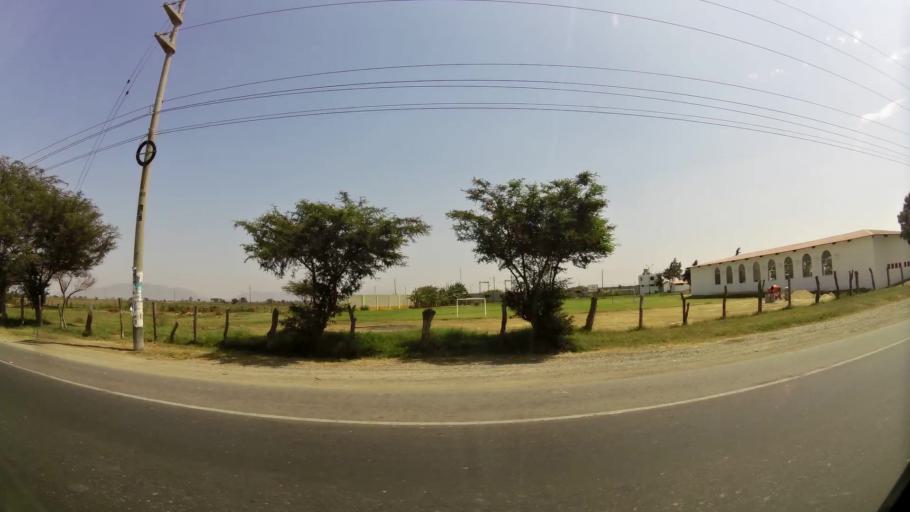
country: PE
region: La Libertad
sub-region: Chepen
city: Chepen
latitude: -7.1939
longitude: -79.4295
